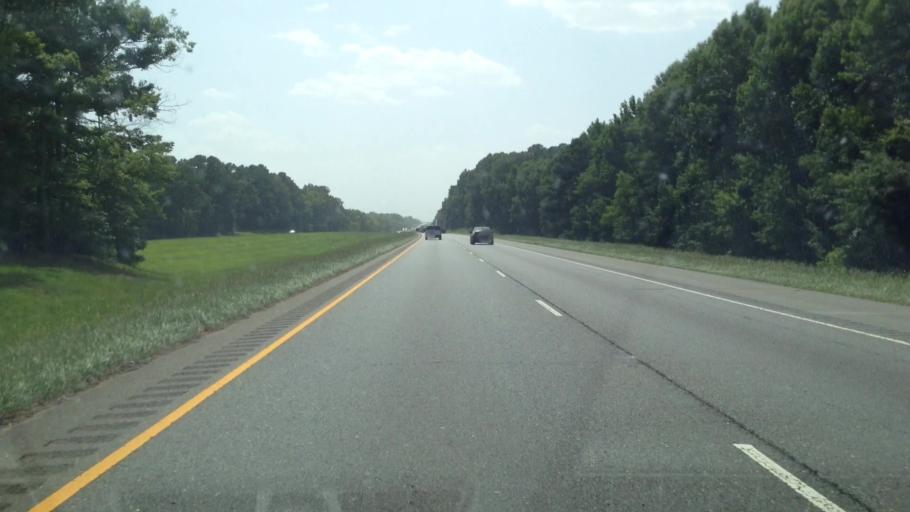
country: US
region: Louisiana
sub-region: Bossier Parish
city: Eastwood
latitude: 32.5423
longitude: -93.5671
